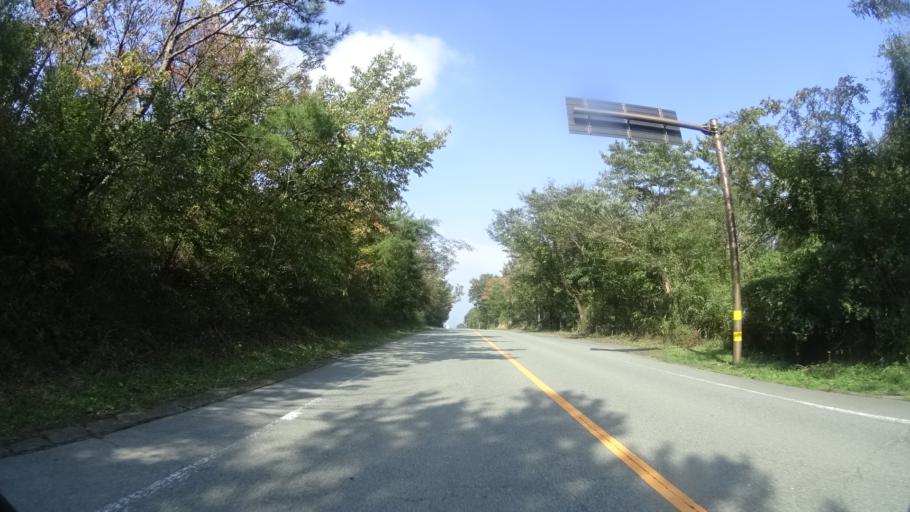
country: JP
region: Kumamoto
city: Aso
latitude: 33.0307
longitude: 131.0638
